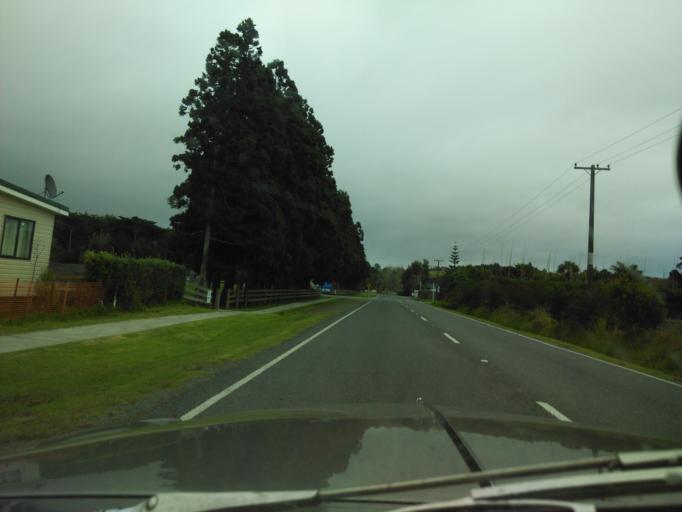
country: NZ
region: Auckland
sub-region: Auckland
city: Wellsford
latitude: -36.1278
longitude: 174.5689
